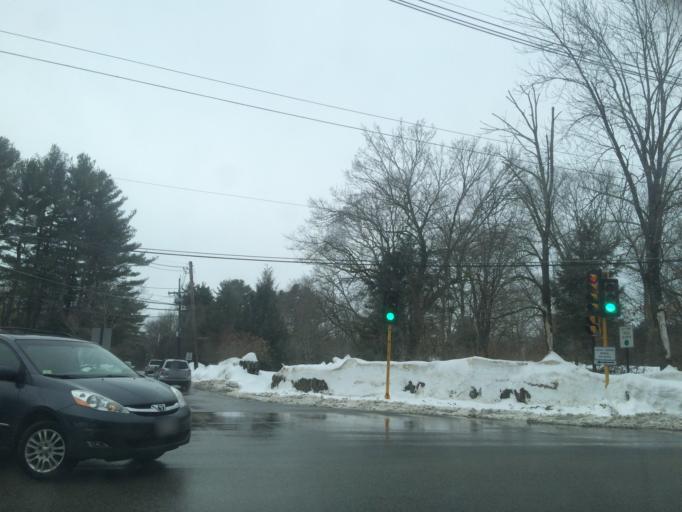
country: US
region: Massachusetts
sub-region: Middlesex County
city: Lincoln
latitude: 42.4146
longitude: -71.3416
